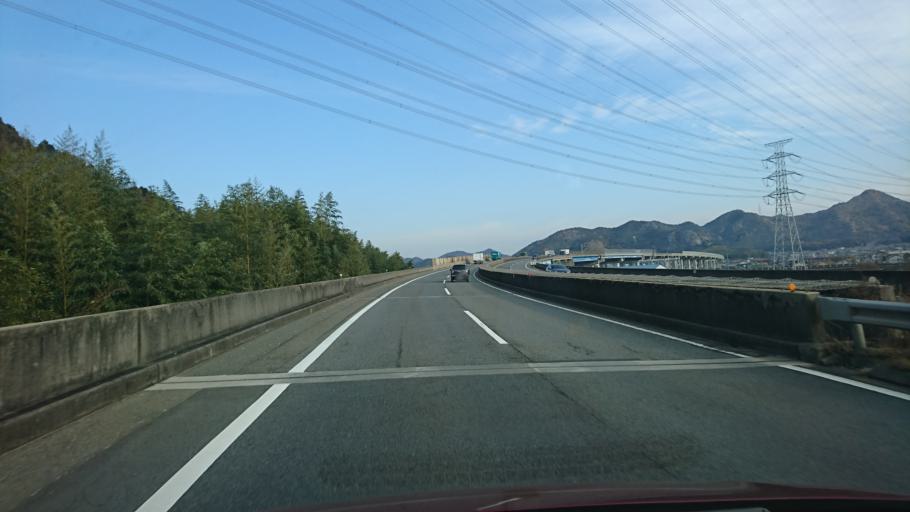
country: JP
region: Hyogo
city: Shirahamacho-usazakiminami
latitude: 34.8074
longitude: 134.7430
